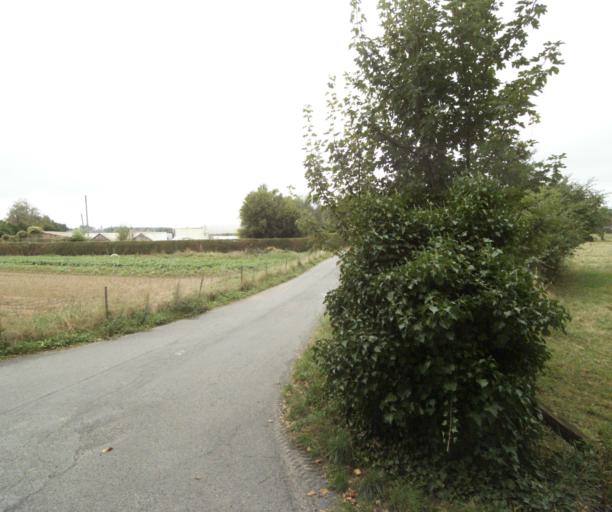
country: FR
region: Nord-Pas-de-Calais
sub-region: Departement du Nord
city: Chereng
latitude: 50.6169
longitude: 3.2192
